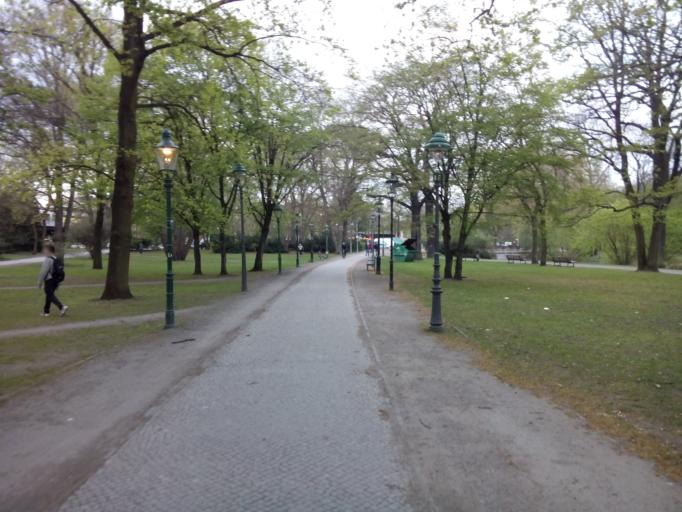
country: DE
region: Berlin
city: Hansaviertel
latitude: 52.5123
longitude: 13.3371
